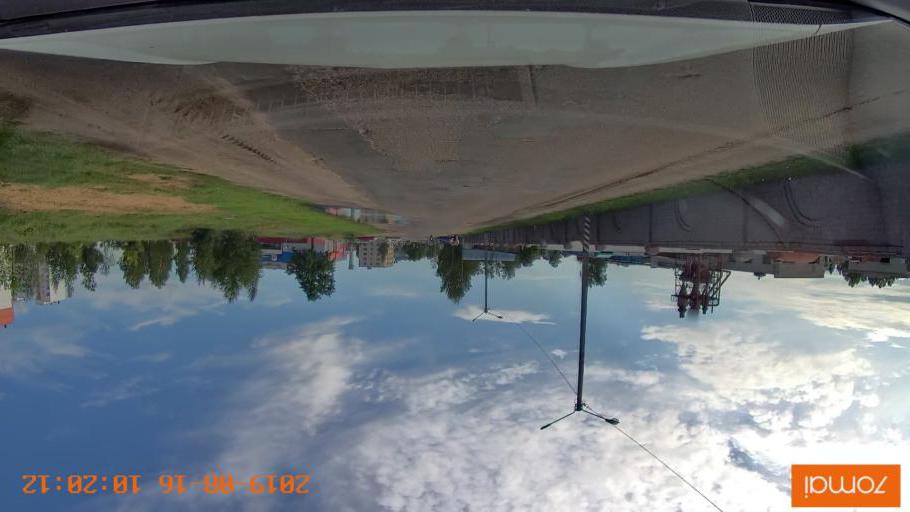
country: BY
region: Mogilev
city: Asipovichy
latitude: 53.3023
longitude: 28.6628
